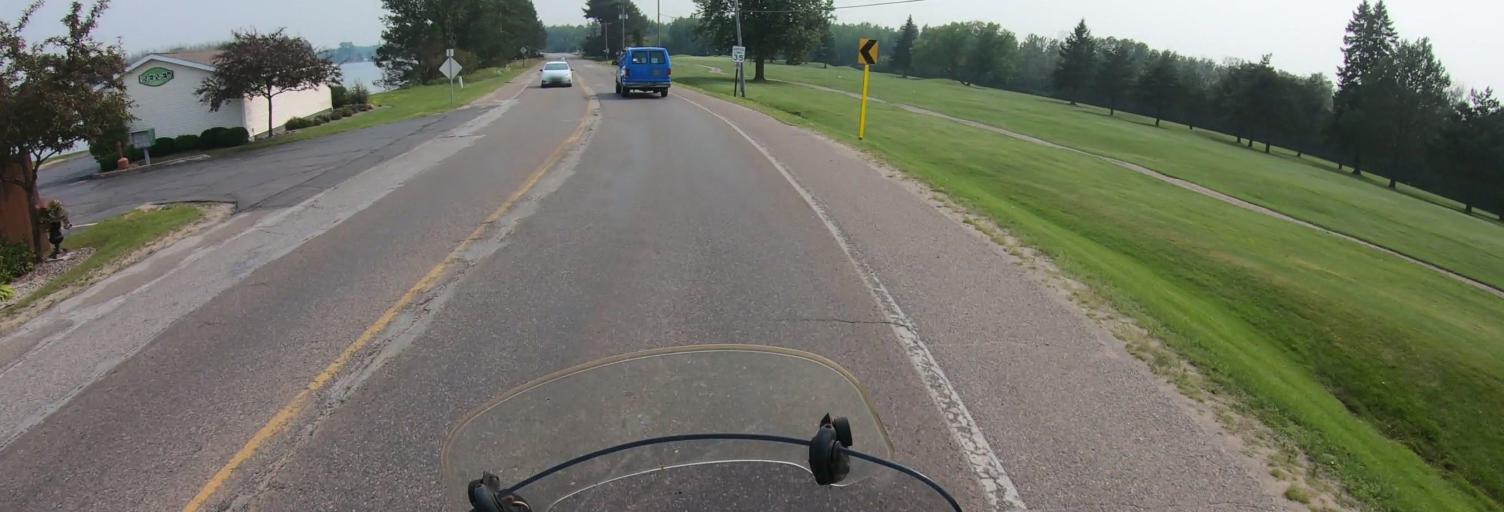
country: US
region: Michigan
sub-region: Chippewa County
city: Sault Ste. Marie
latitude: 46.4815
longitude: -84.3038
